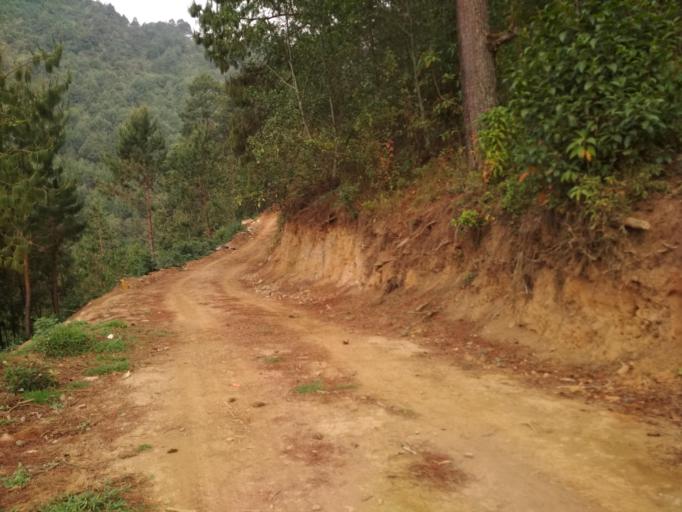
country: MX
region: Veracruz
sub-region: Camerino Z. Mendoza
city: Necoxtla
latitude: 18.7545
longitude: -97.1594
